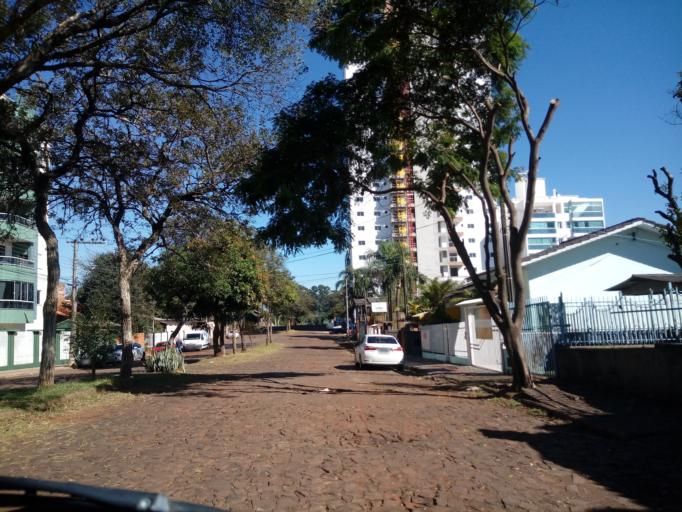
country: BR
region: Santa Catarina
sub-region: Chapeco
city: Chapeco
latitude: -27.1008
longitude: -52.6234
